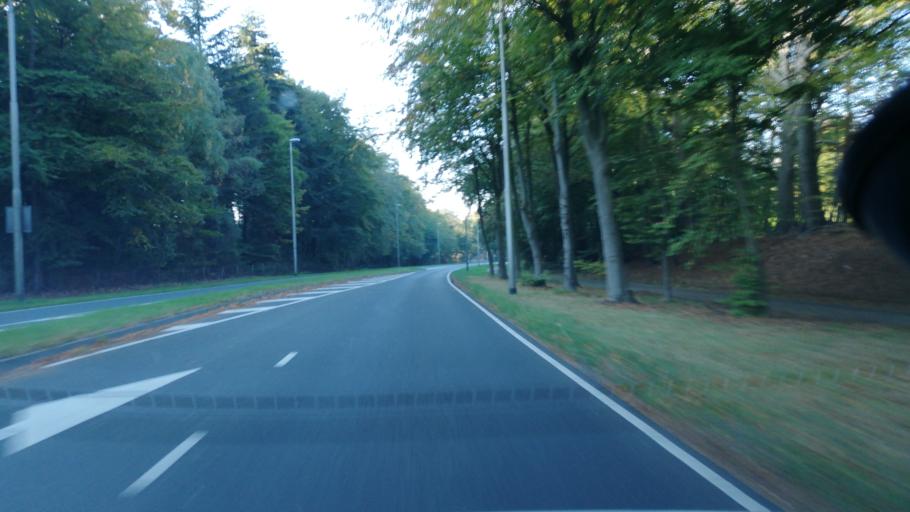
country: NL
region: Gelderland
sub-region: Gemeente Arnhem
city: Arnhem
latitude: 52.0010
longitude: 5.9198
